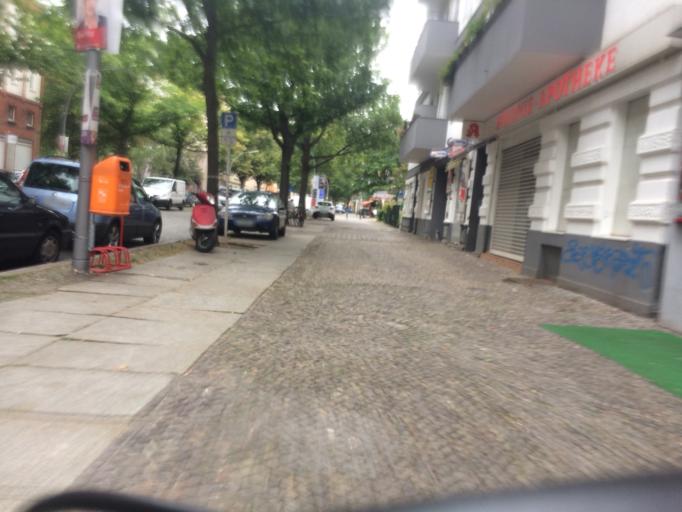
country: DE
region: Berlin
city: Gesundbrunnen
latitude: 52.5578
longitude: 13.3785
